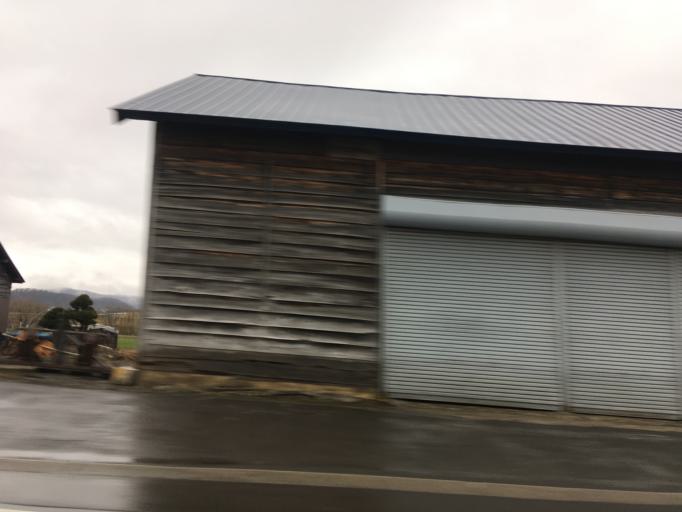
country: JP
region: Hokkaido
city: Nayoro
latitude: 44.1096
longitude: 142.4786
